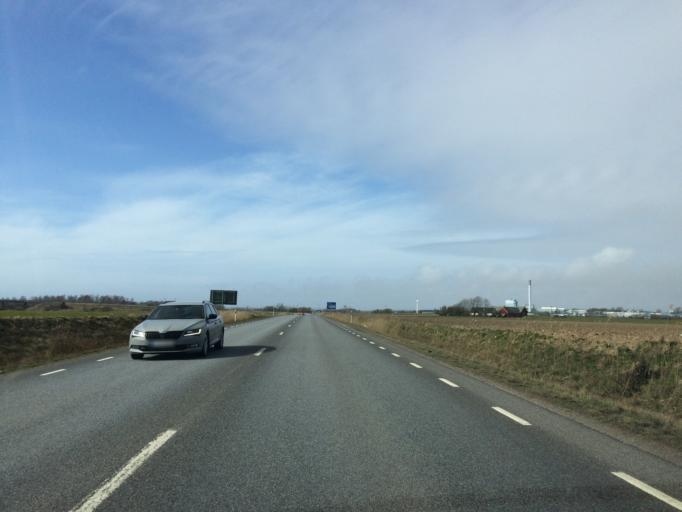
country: SE
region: Halland
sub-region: Halmstads Kommun
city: Troenninge
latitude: 56.6241
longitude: 12.9500
